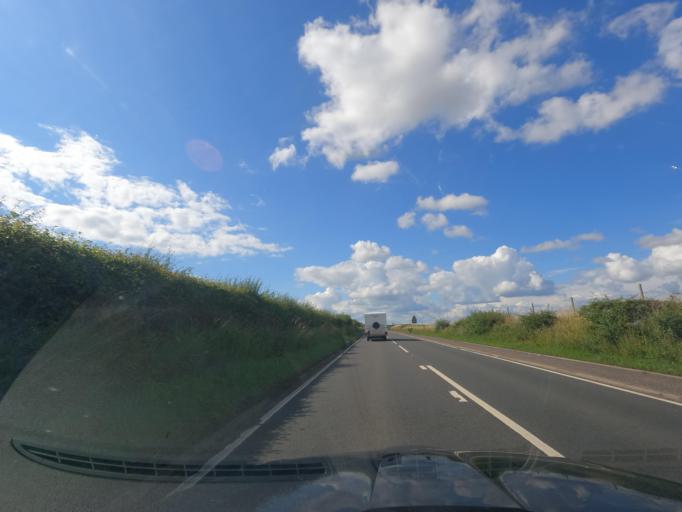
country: GB
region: Scotland
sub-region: Fife
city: Pathhead
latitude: 55.8396
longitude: -2.9169
